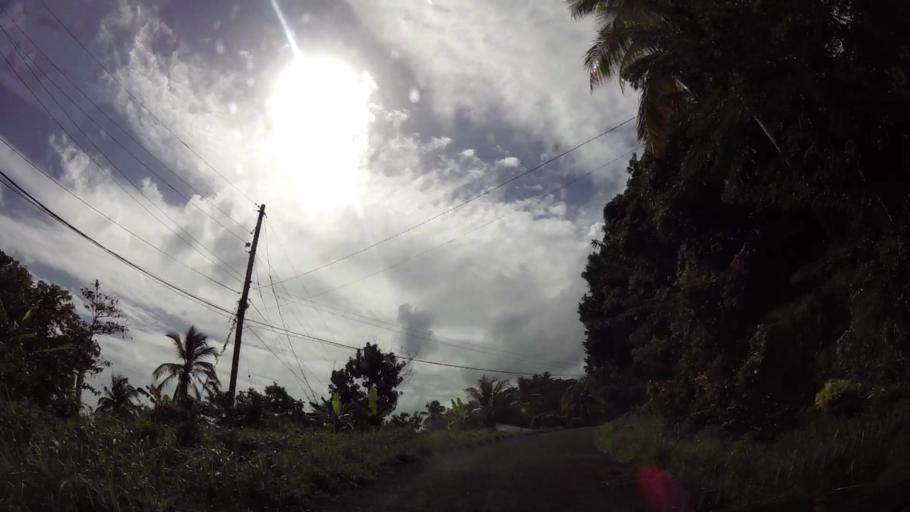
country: DM
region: Saint David
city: Castle Bruce
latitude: 15.4699
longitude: -61.2489
